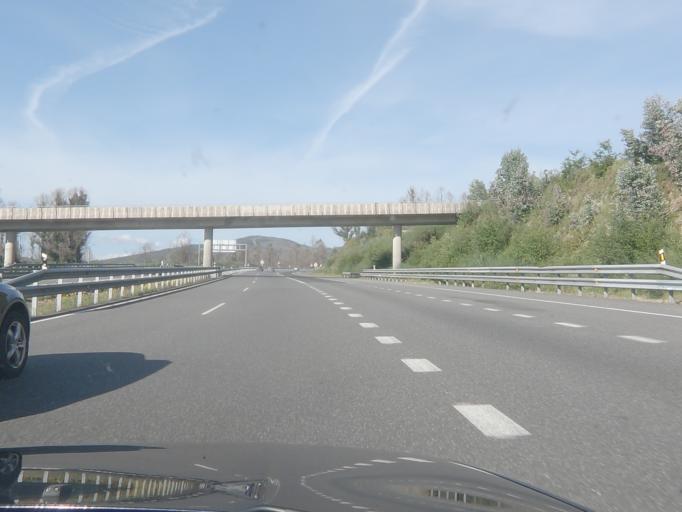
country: ES
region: Galicia
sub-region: Provincia de Pontevedra
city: Ponteareas
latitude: 42.1506
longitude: -8.4255
